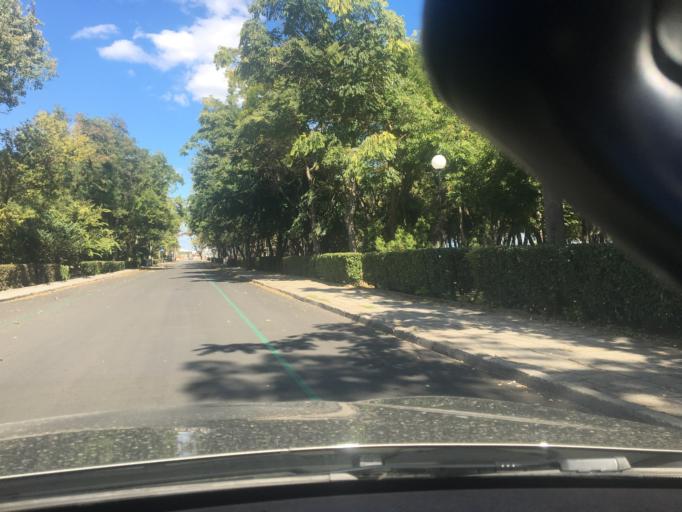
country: BG
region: Burgas
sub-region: Obshtina Burgas
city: Burgas
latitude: 42.5070
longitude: 27.4820
